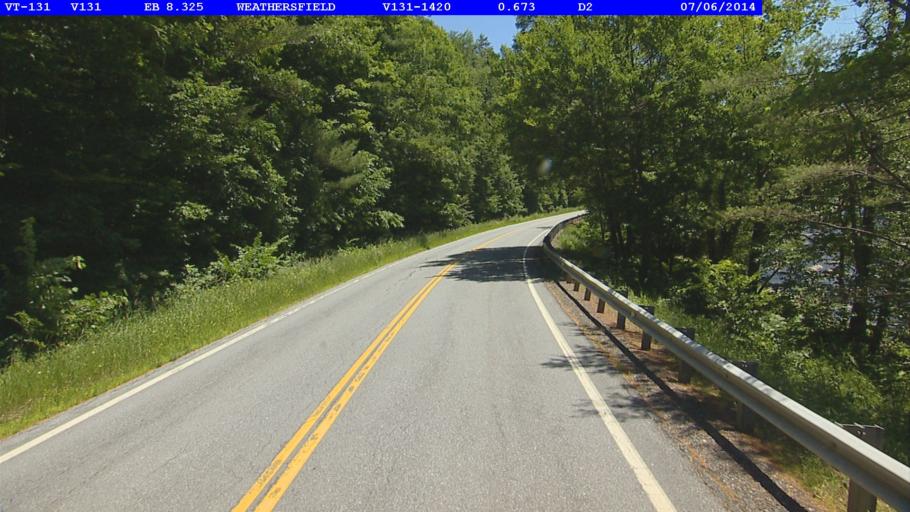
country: US
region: Vermont
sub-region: Windsor County
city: Springfield
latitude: 43.3998
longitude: -72.5279
